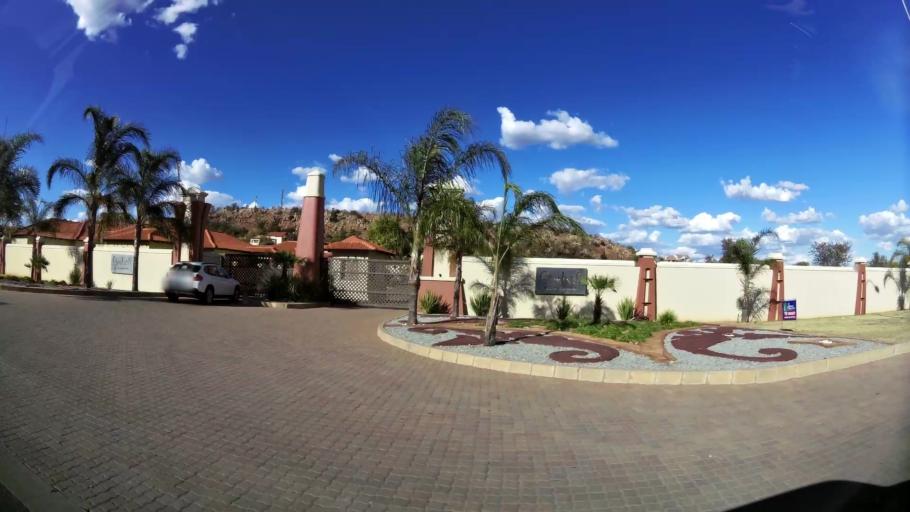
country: ZA
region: North-West
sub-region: Dr Kenneth Kaunda District Municipality
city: Klerksdorp
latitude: -26.8196
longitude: 26.6792
